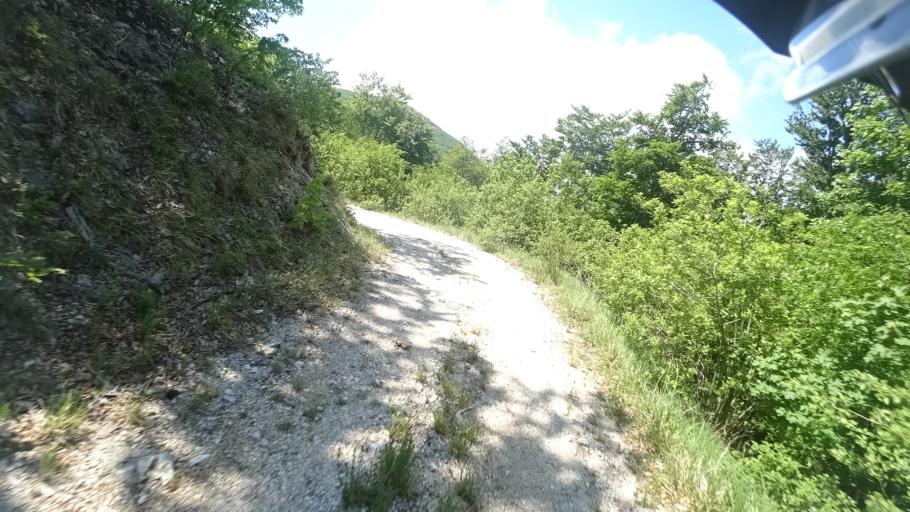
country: BA
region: Federation of Bosnia and Herzegovina
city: Orasac
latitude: 44.5707
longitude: 15.8532
